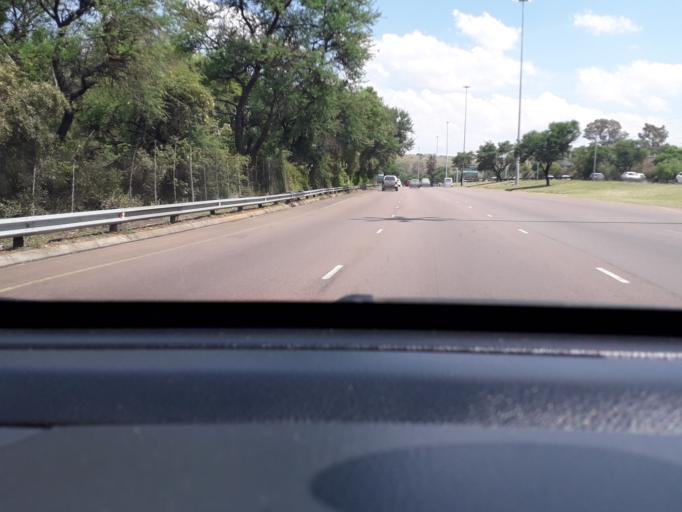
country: ZA
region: Gauteng
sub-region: City of Tshwane Metropolitan Municipality
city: Pretoria
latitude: -25.7760
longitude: 28.1943
